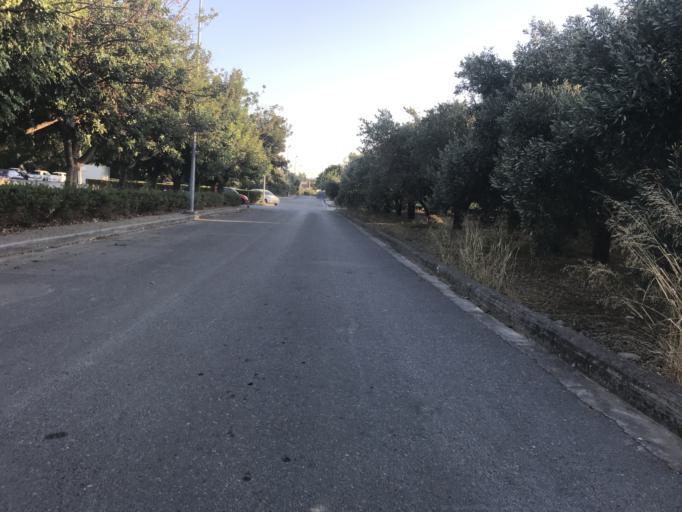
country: GR
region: Crete
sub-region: Nomos Irakleiou
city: Gazi
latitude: 35.3061
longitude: 25.0731
